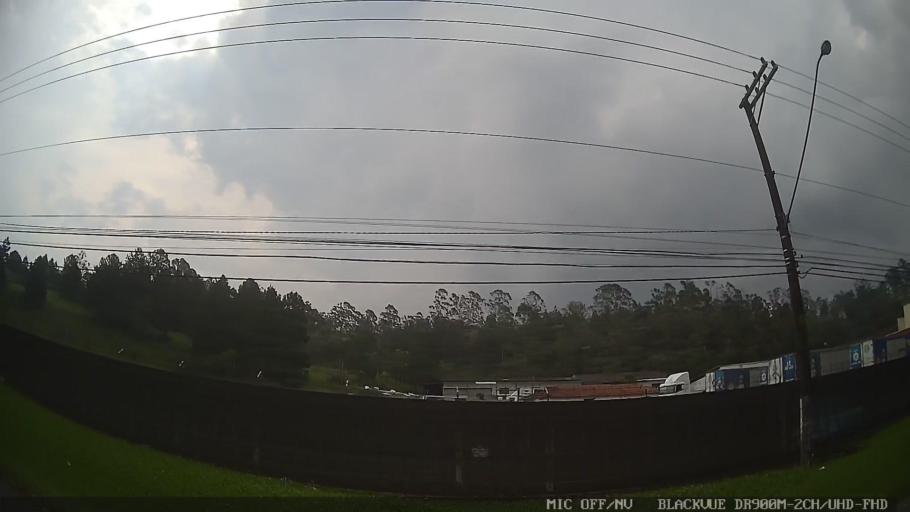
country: BR
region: Sao Paulo
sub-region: Ribeirao Pires
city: Ribeirao Pires
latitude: -23.6591
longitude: -46.3761
